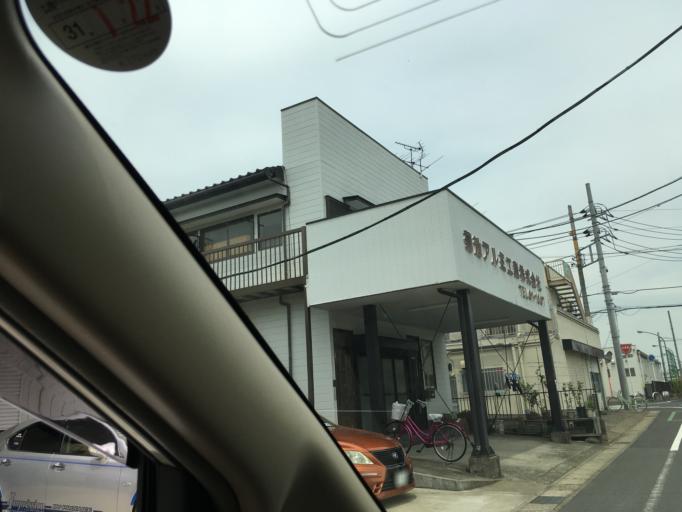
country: JP
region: Chiba
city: Matsudo
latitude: 35.8084
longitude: 139.8996
